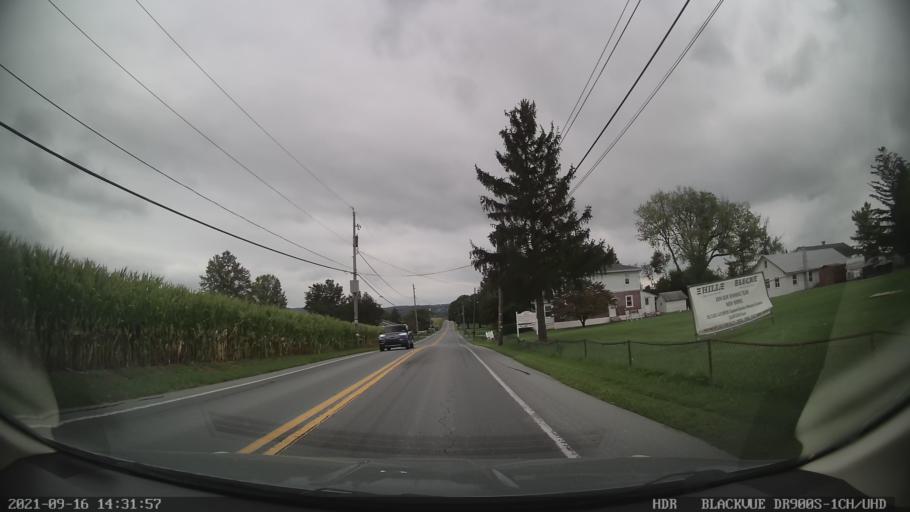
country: US
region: Pennsylvania
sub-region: Berks County
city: Kutztown
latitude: 40.5021
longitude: -75.7673
